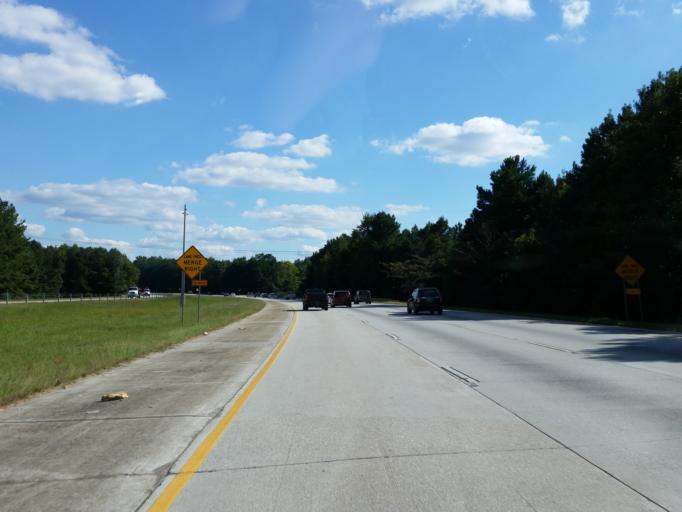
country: US
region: Georgia
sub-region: Clayton County
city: Lake City
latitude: 33.6051
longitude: -84.2953
